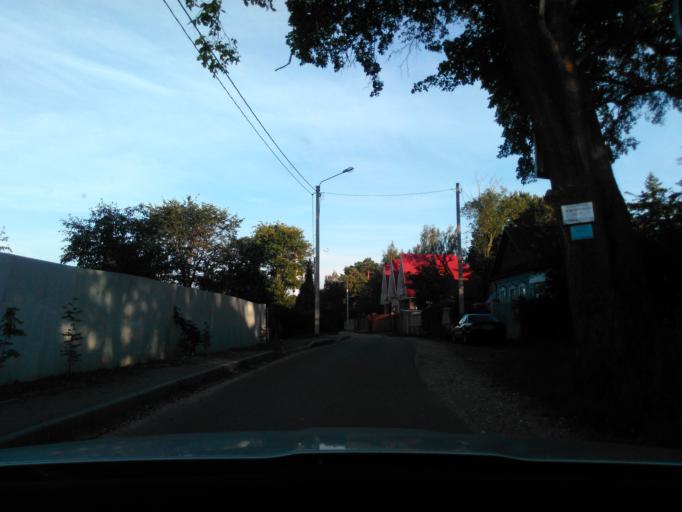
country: RU
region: Tverskaya
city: Konakovo
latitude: 56.7542
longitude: 36.7531
